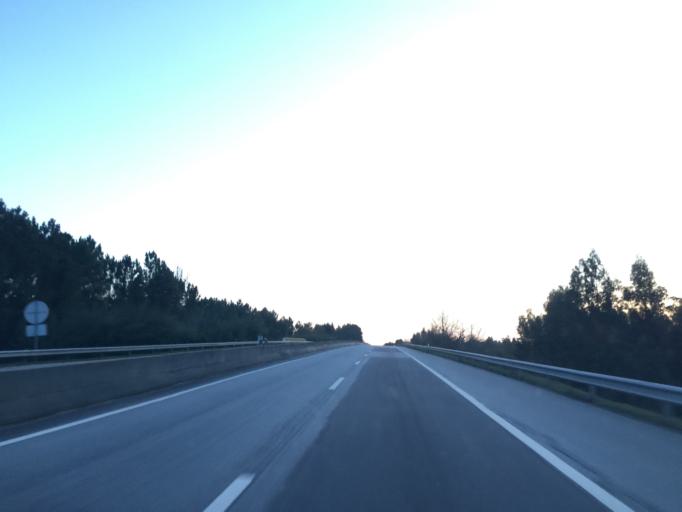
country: PT
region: Viseu
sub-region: Concelho de Carregal do Sal
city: Carregal do Sal
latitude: 40.4272
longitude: -8.0235
